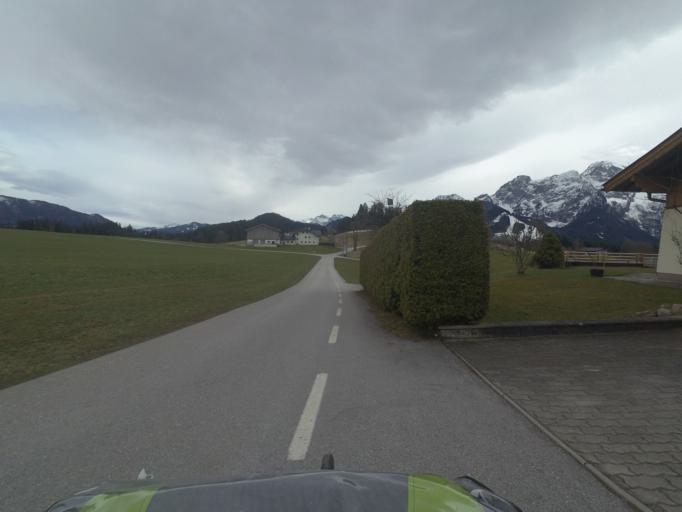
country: AT
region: Salzburg
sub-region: Politischer Bezirk Hallein
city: Abtenau
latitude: 47.5774
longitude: 13.3336
